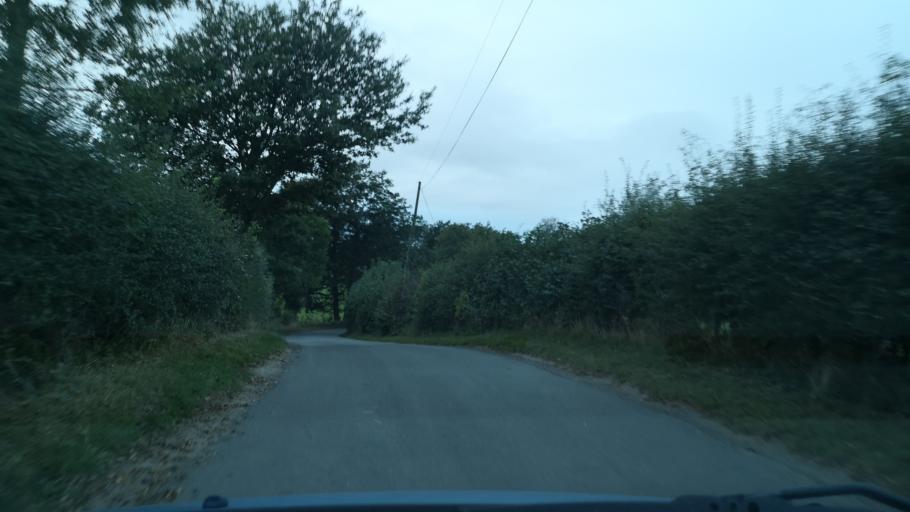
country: GB
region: England
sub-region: City and Borough of Wakefield
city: Low Ackworth
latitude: 53.6586
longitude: -1.3170
